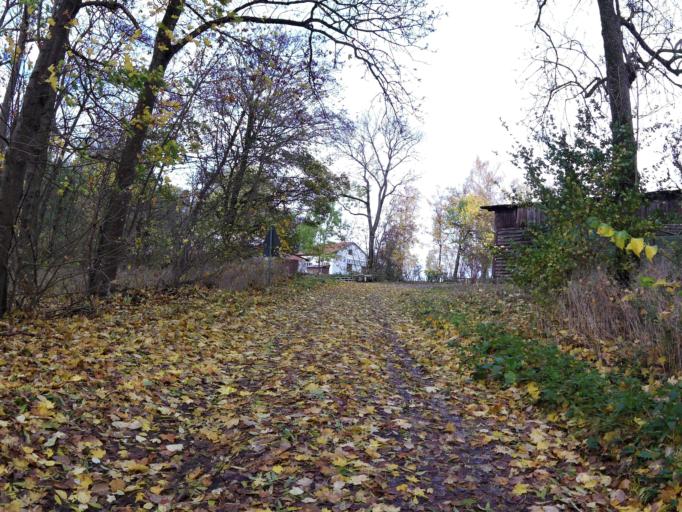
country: DE
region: Hesse
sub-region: Regierungsbezirk Kassel
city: Herleshausen
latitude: 51.0535
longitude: 10.1270
